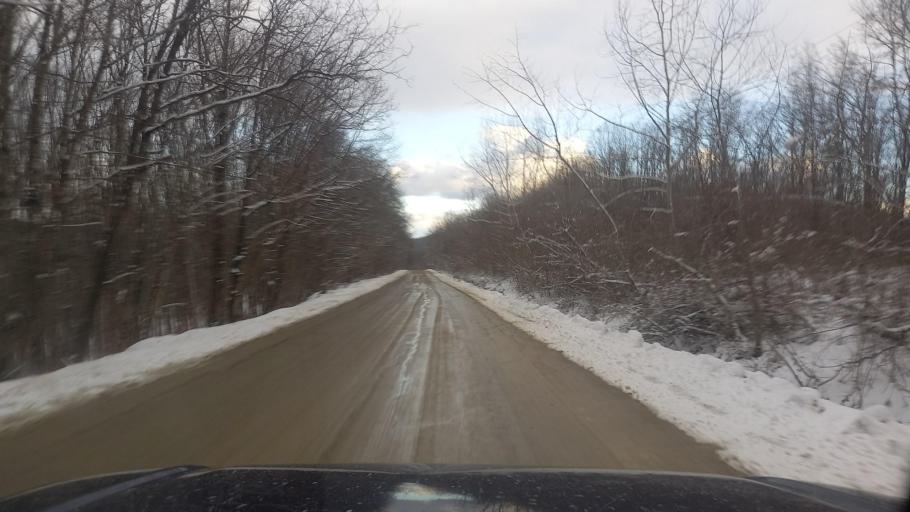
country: RU
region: Krasnodarskiy
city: Smolenskaya
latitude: 44.6756
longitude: 38.7360
